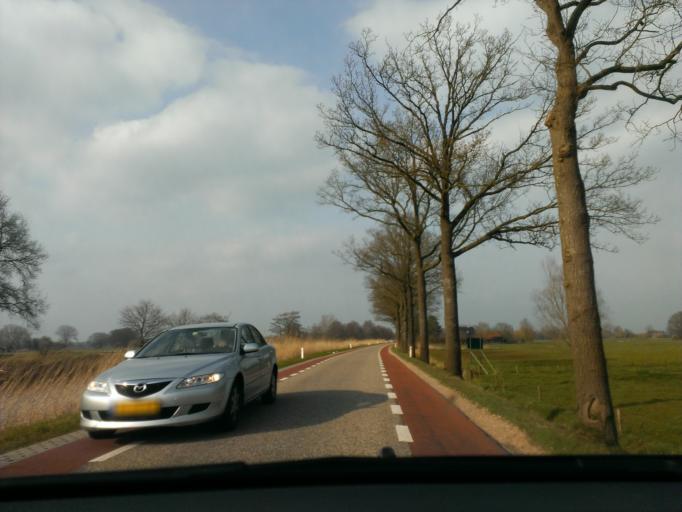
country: NL
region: Gelderland
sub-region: Gemeente Epe
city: Vaassen
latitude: 52.2571
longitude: 5.9828
